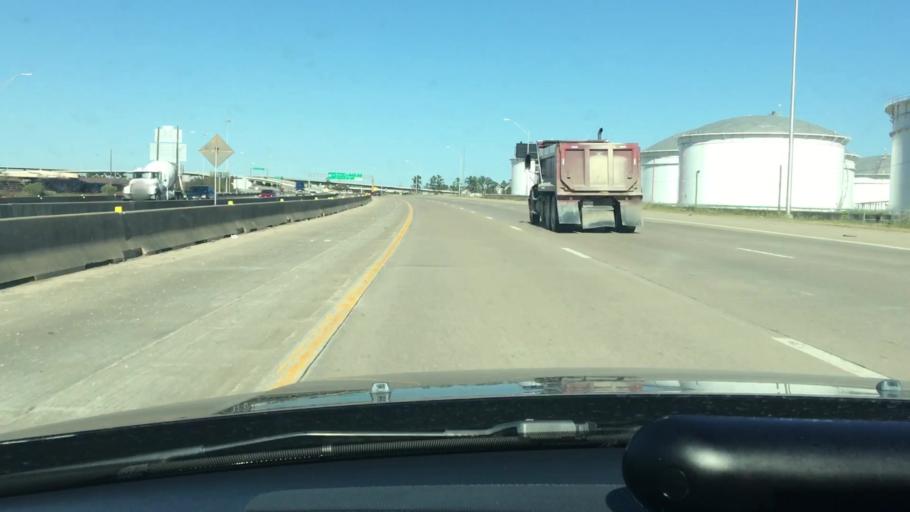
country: US
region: Texas
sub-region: Harris County
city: Cloverleaf
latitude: 29.7615
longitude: -95.1465
